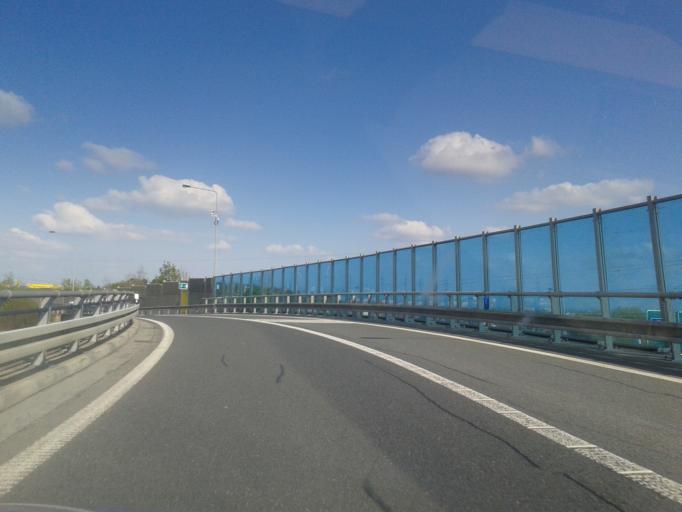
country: CZ
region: Central Bohemia
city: Hostivice
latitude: 50.0471
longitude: 14.2721
